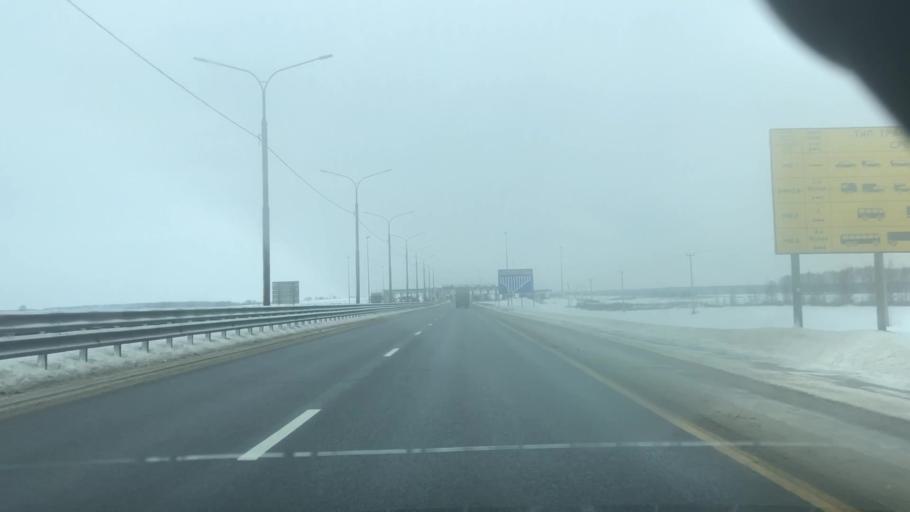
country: RU
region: Tula
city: Dubovka
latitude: 53.8830
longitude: 38.0508
